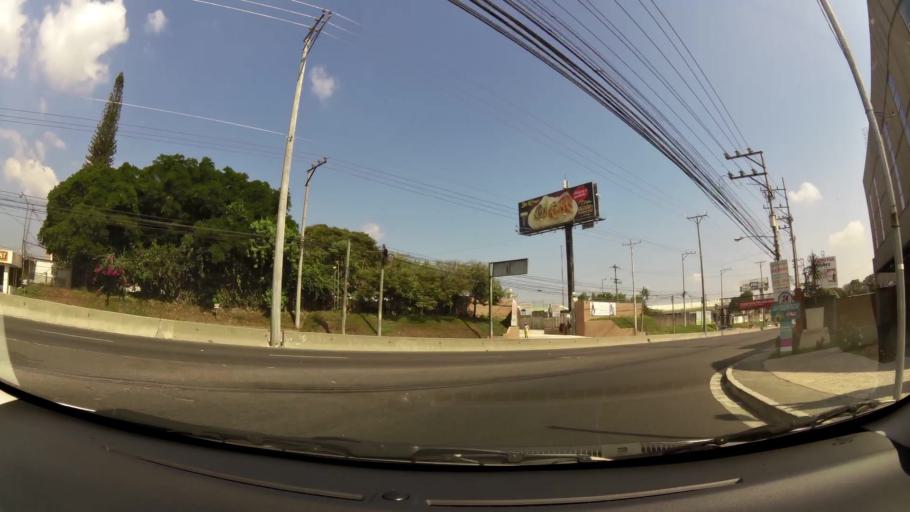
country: SV
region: La Libertad
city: Santa Tecla
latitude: 13.6676
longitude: -89.2702
